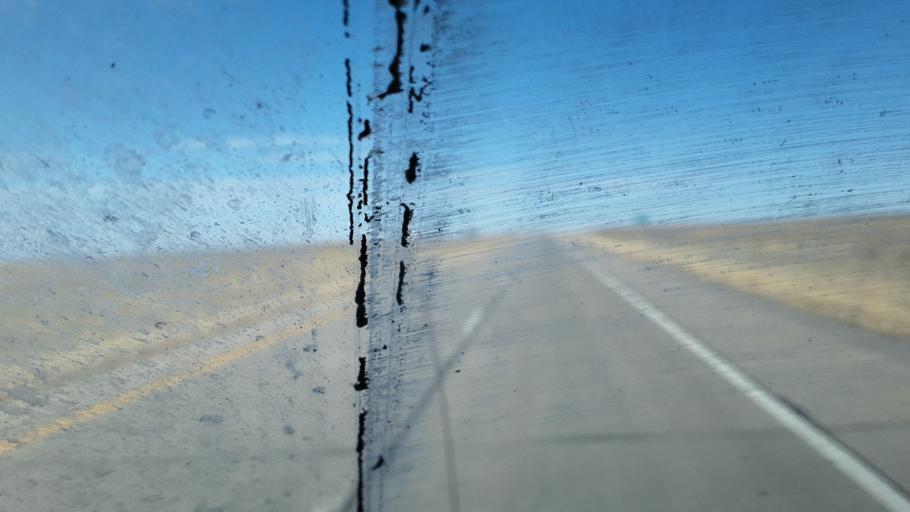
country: US
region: Colorado
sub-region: Weld County
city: Keenesburg
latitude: 40.1868
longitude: -104.2979
